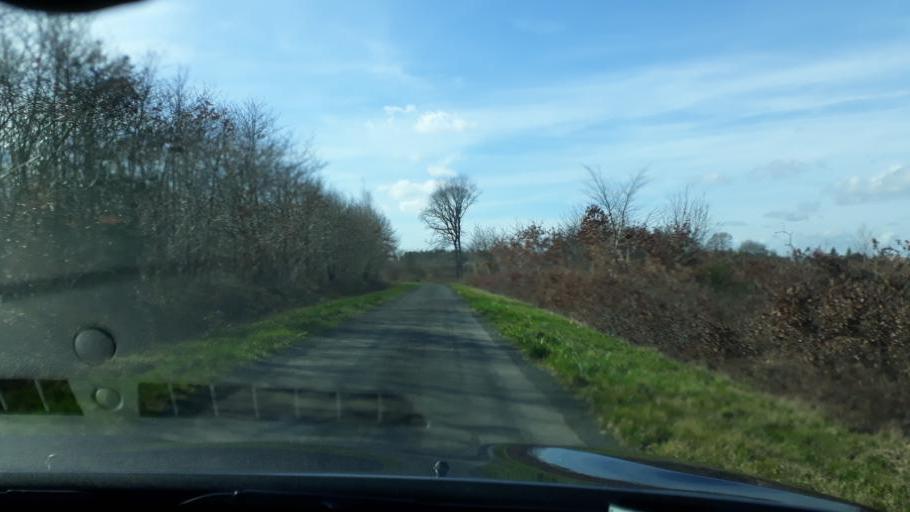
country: FR
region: Centre
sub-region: Departement du Loiret
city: Trainou
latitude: 47.9903
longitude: 2.1213
